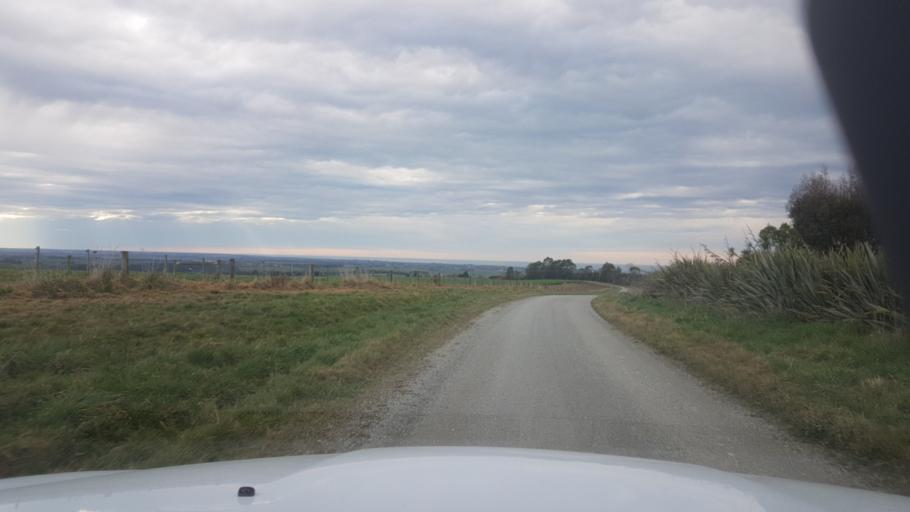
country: NZ
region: Canterbury
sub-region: Timaru District
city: Pleasant Point
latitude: -44.3455
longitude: 171.1253
